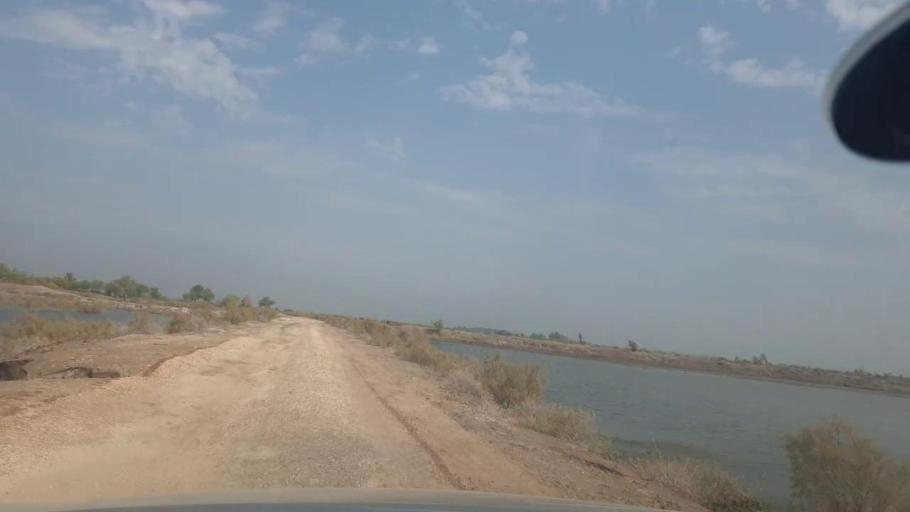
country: PK
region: Balochistan
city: Mehrabpur
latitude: 28.0326
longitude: 68.1298
